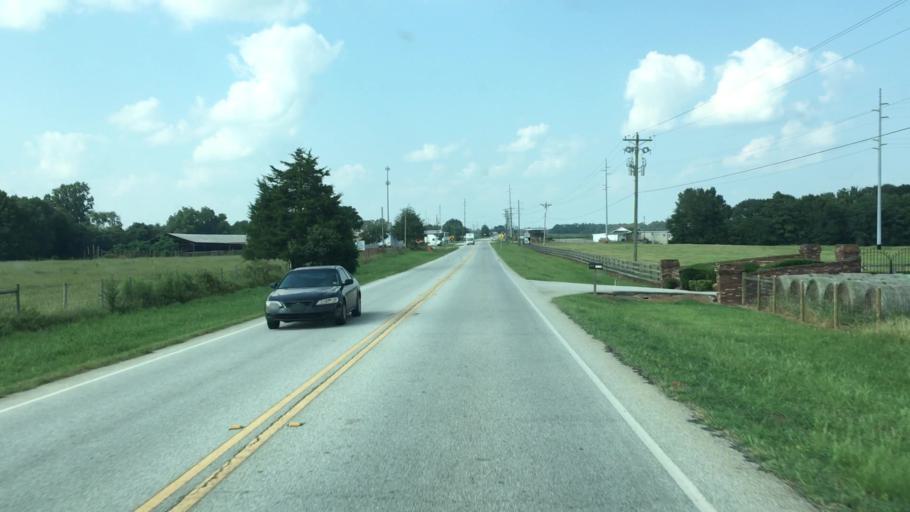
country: US
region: Georgia
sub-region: Walton County
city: Social Circle
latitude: 33.5490
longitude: -83.7401
